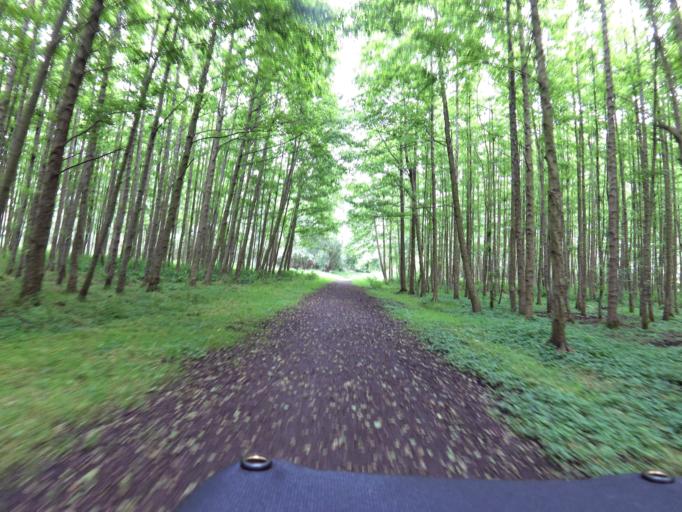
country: NL
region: South Holland
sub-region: Gemeente Hellevoetsluis
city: Nieuwenhoorn
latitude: 51.8543
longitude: 4.1534
